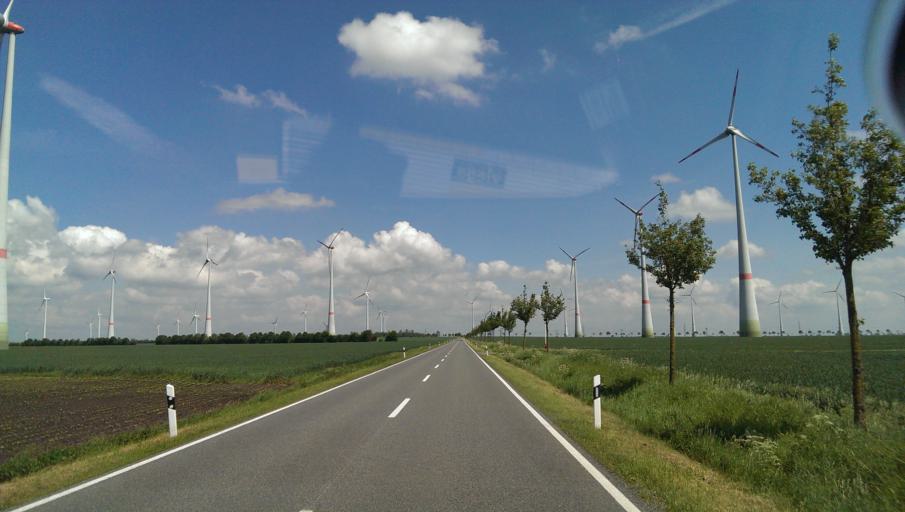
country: DE
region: Saxony-Anhalt
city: Borne
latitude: 51.9524
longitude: 11.5885
